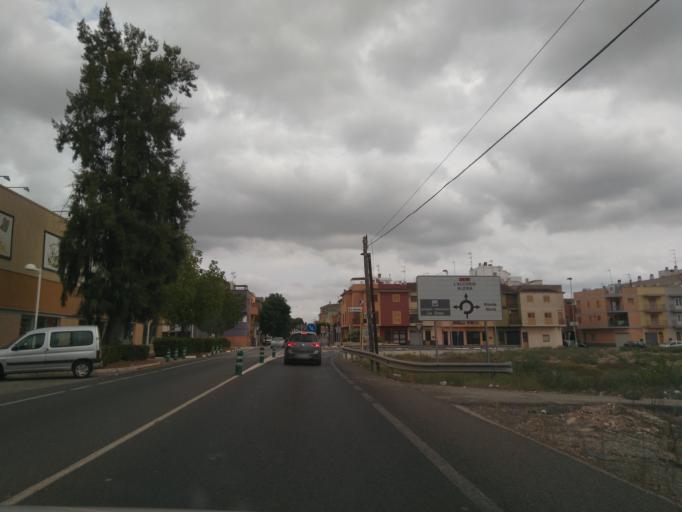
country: ES
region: Valencia
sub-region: Provincia de Valencia
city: L'Alcudia
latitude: 39.2026
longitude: -0.5068
